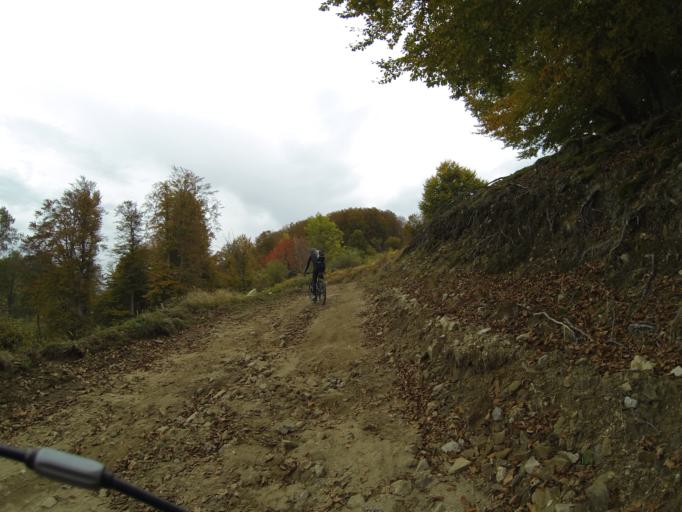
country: RO
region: Gorj
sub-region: Comuna Tismana
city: Sohodol
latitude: 45.1261
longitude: 22.8623
